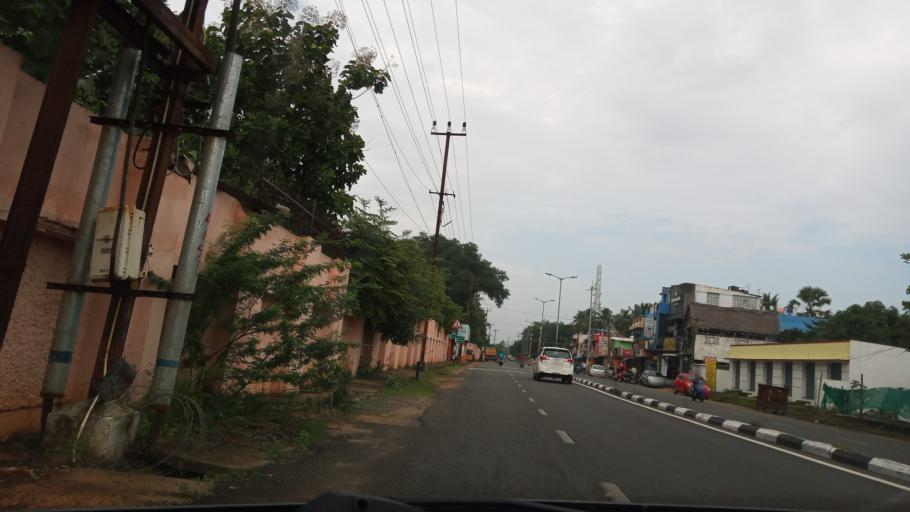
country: IN
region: Tamil Nadu
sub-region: Villupuram
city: Auroville
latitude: 12.0150
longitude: 79.8583
